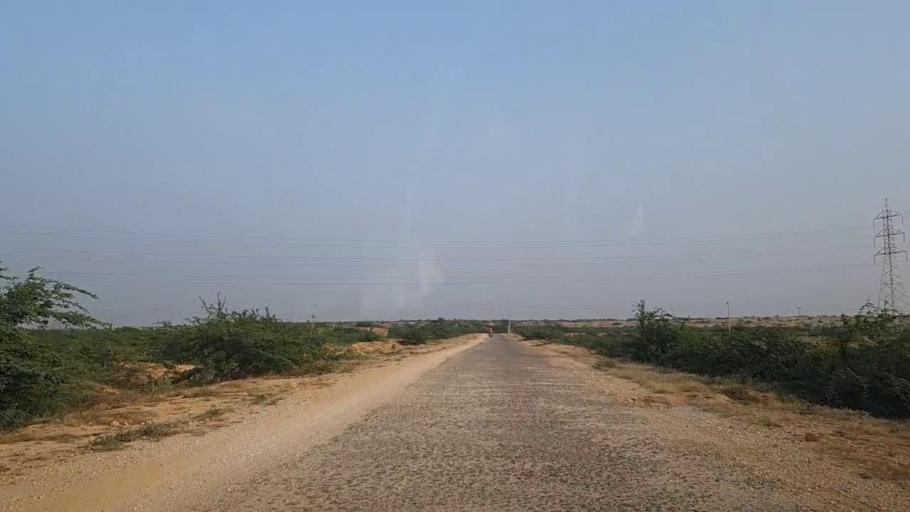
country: PK
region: Sindh
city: Thatta
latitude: 24.6889
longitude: 67.8508
